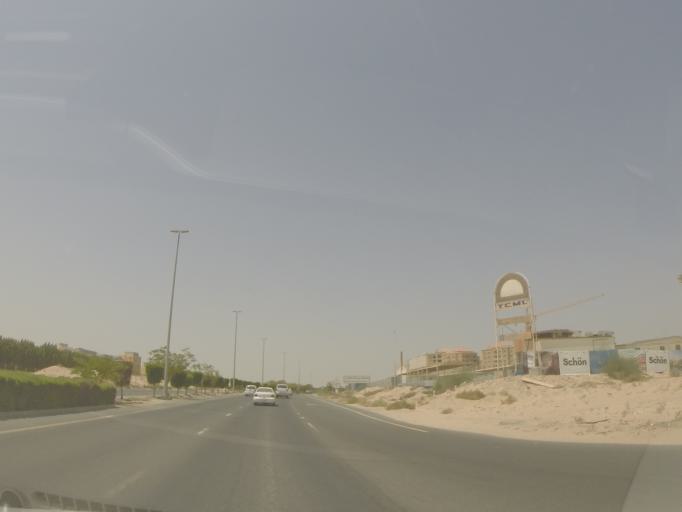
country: AE
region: Dubai
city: Dubai
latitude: 24.9880
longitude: 55.1852
